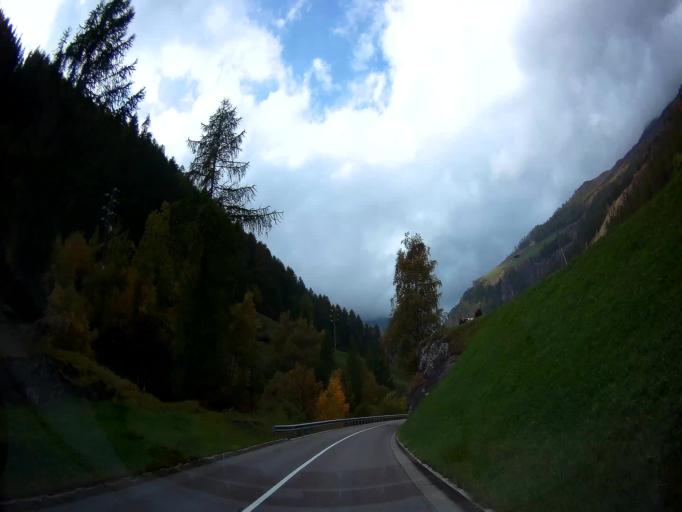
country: IT
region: Trentino-Alto Adige
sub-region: Bolzano
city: Senales
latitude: 46.7117
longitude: 10.8964
